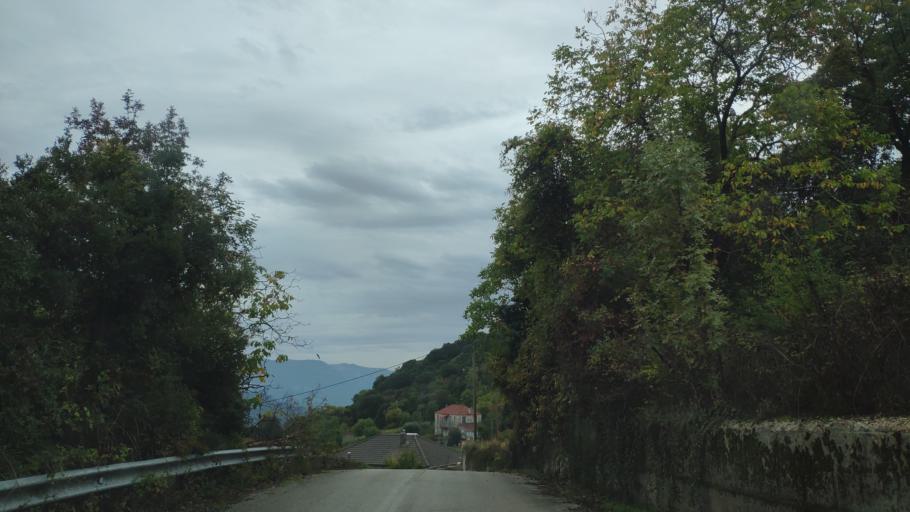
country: GR
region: Epirus
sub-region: Nomos Thesprotias
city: Paramythia
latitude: 39.4591
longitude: 20.6709
